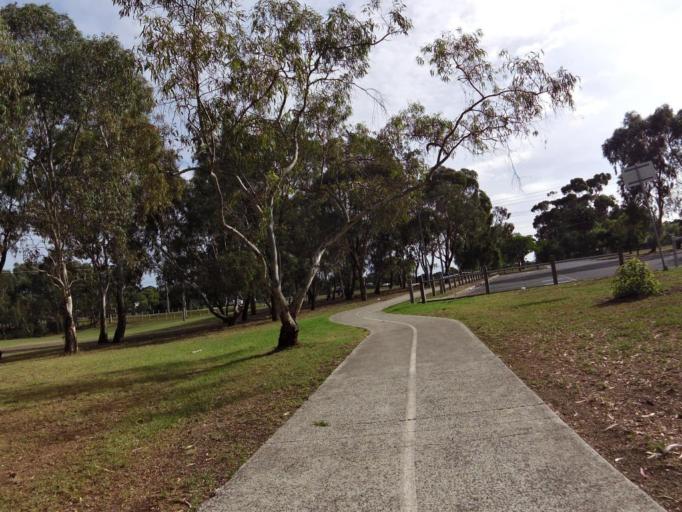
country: AU
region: Victoria
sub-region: Moreland
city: Glenroy
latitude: -37.6883
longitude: 144.9377
